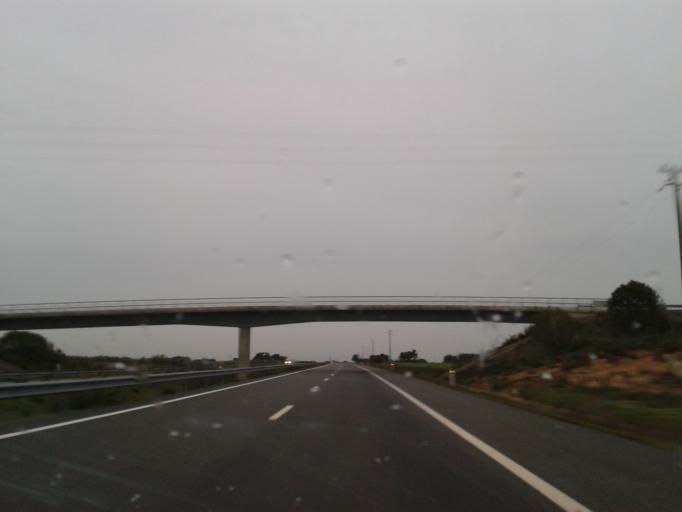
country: PT
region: Beja
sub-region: Aljustrel
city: Aljustrel
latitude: 38.0273
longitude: -8.2878
